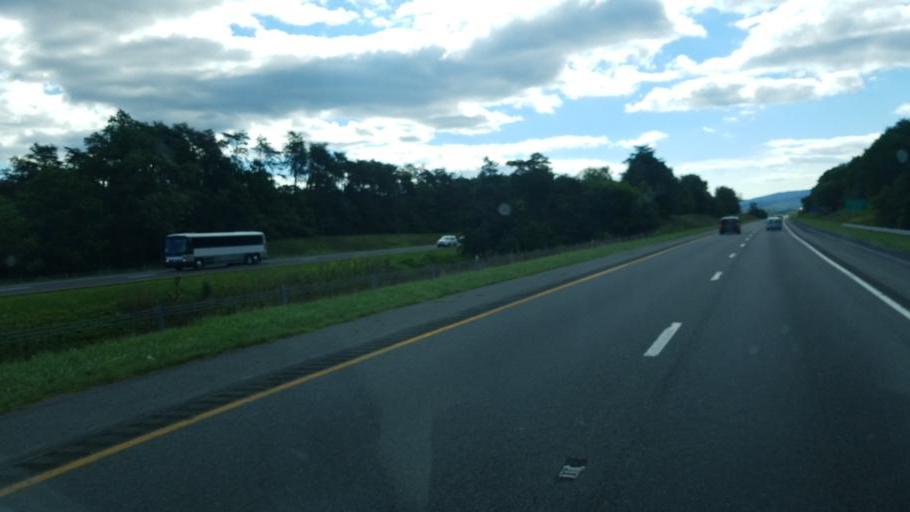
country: US
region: Virginia
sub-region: Warren County
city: Front Royal
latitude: 38.9714
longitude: -78.2100
